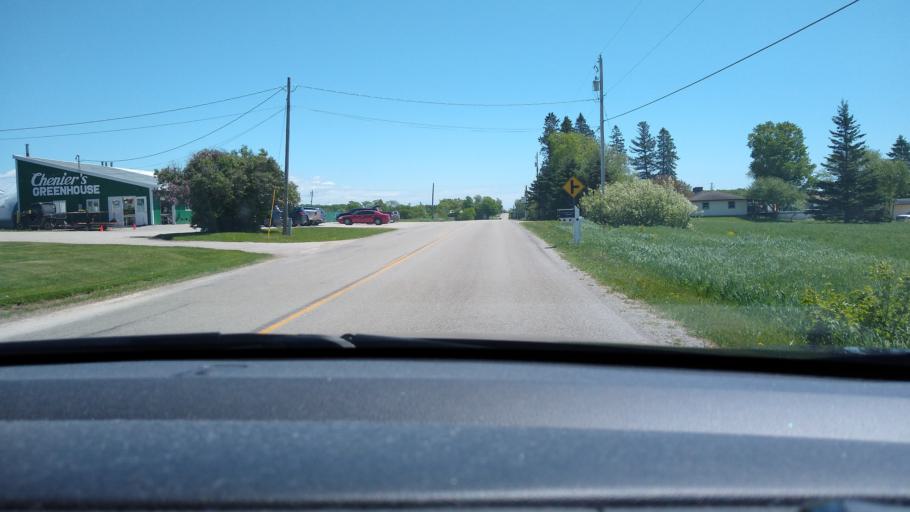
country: US
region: Michigan
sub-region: Delta County
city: Escanaba
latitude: 45.8261
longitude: -87.1447
